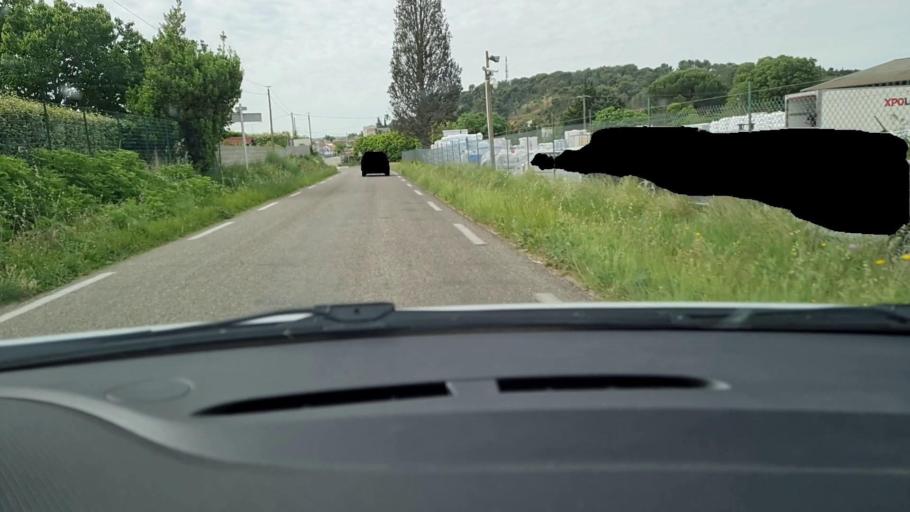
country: FR
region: Languedoc-Roussillon
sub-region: Departement du Gard
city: Bellegarde
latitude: 43.7610
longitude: 4.5105
